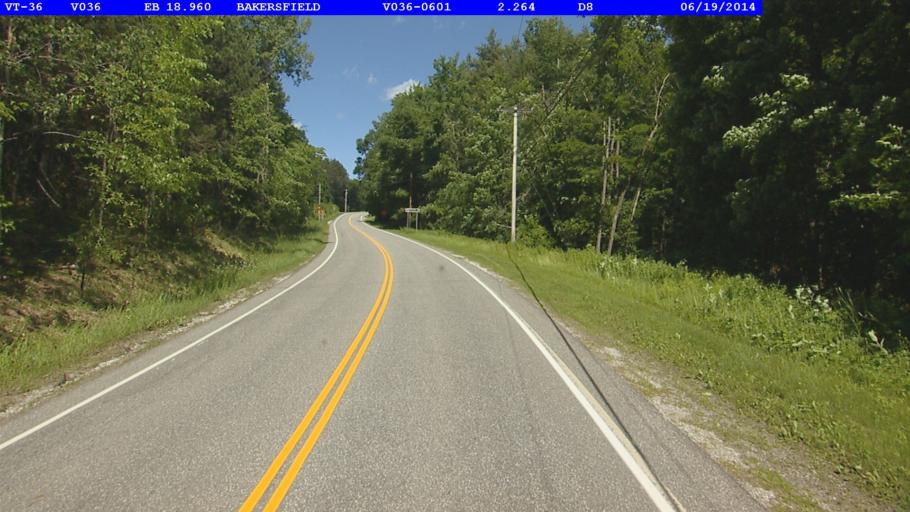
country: US
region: Vermont
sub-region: Franklin County
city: Enosburg Falls
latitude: 44.7806
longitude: -72.8057
